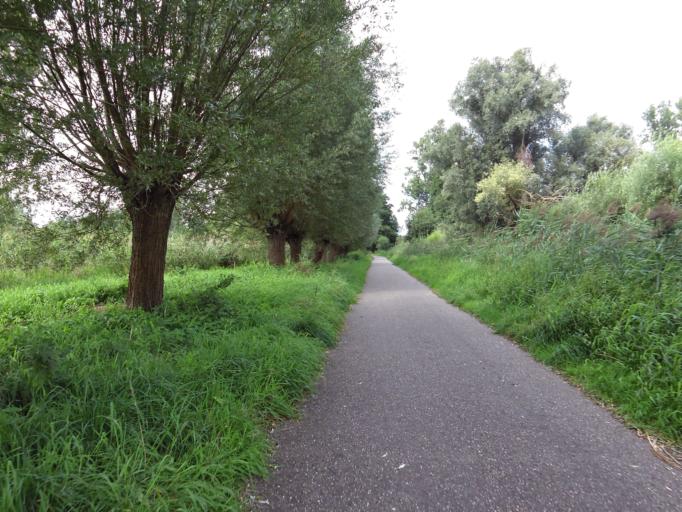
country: DE
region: North Rhine-Westphalia
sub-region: Regierungsbezirk Koln
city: Gangelt
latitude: 50.9837
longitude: 5.9939
